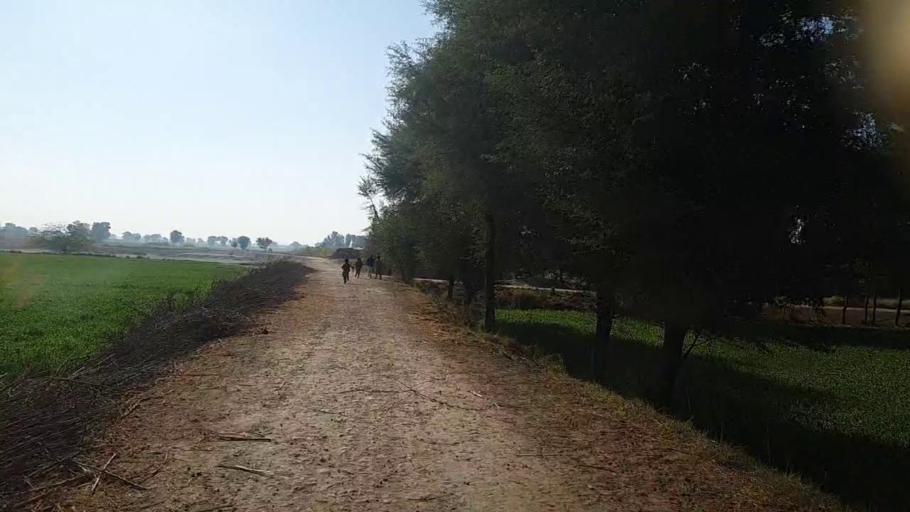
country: PK
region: Sindh
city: Khairpur
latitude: 28.0542
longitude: 69.7483
